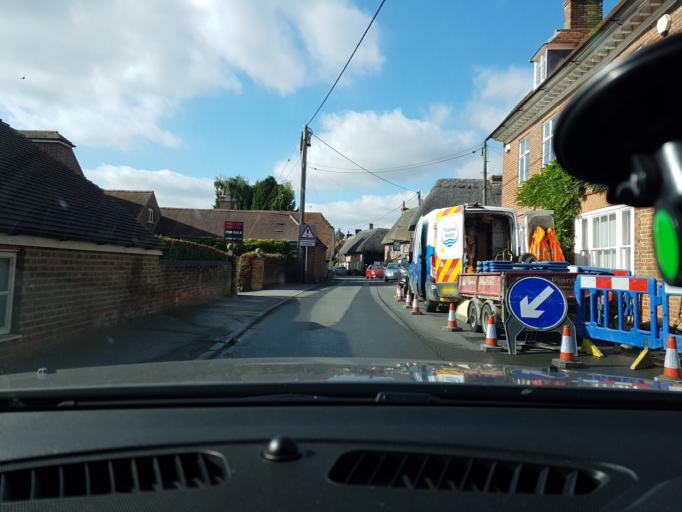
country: GB
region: England
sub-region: Wiltshire
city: Chilton Foliat
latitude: 51.4314
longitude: -1.5379
